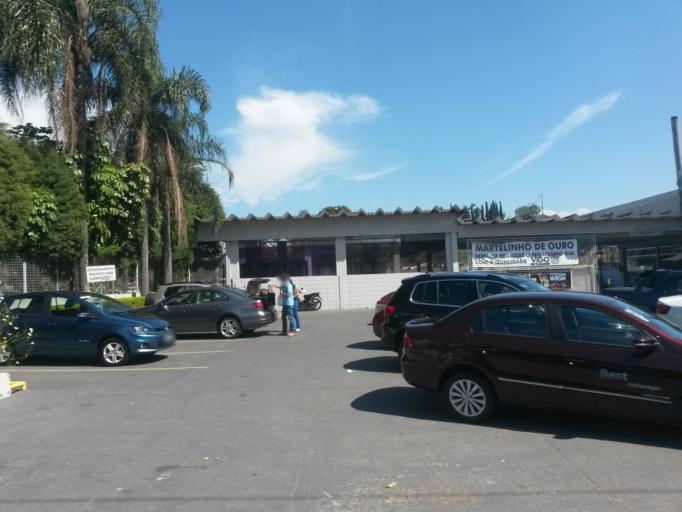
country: BR
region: Sao Paulo
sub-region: Sao Bernardo Do Campo
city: Sao Bernardo do Campo
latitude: -23.7259
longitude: -46.5493
